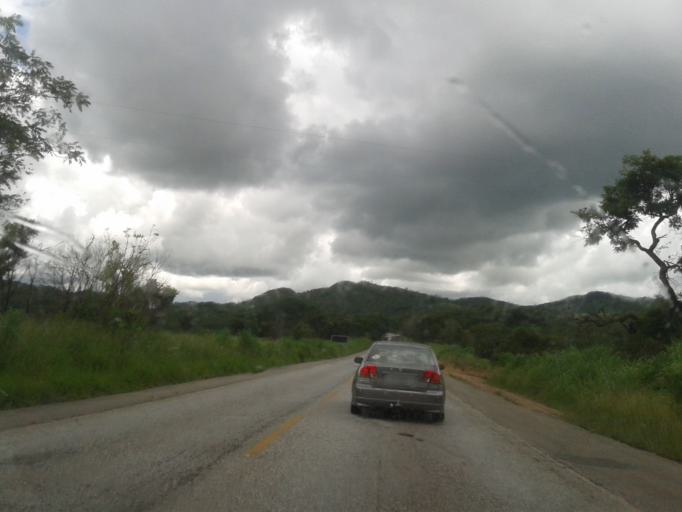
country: BR
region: Goias
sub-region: Goias
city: Goias
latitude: -15.9918
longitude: -50.0752
